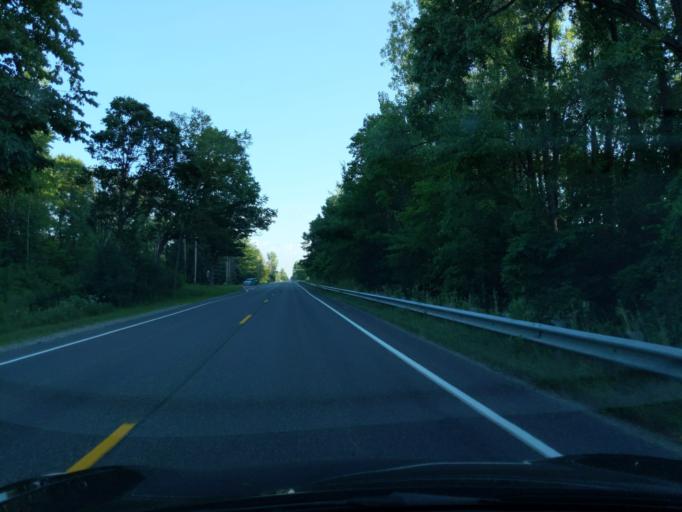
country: US
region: Michigan
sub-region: Midland County
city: Midland
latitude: 43.5555
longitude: -84.3697
